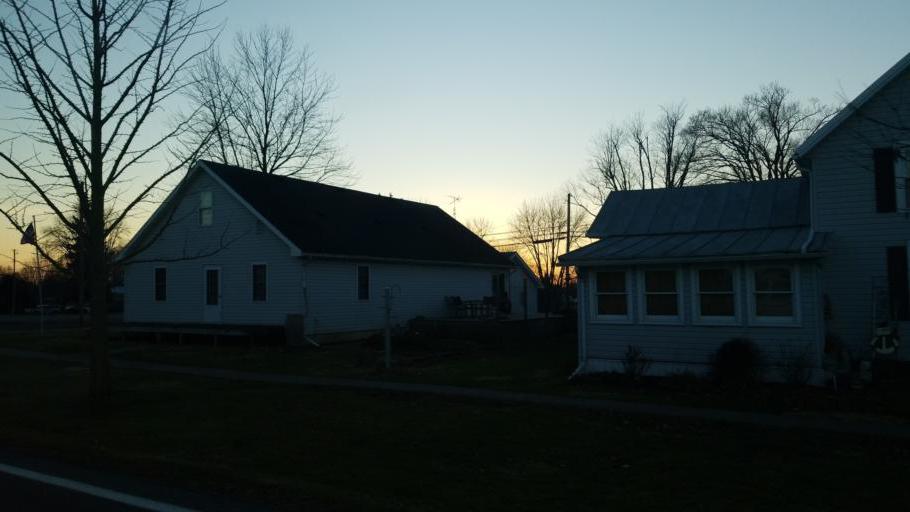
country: US
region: Ohio
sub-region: Wyandot County
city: Upper Sandusky
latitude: 40.8214
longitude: -83.1307
